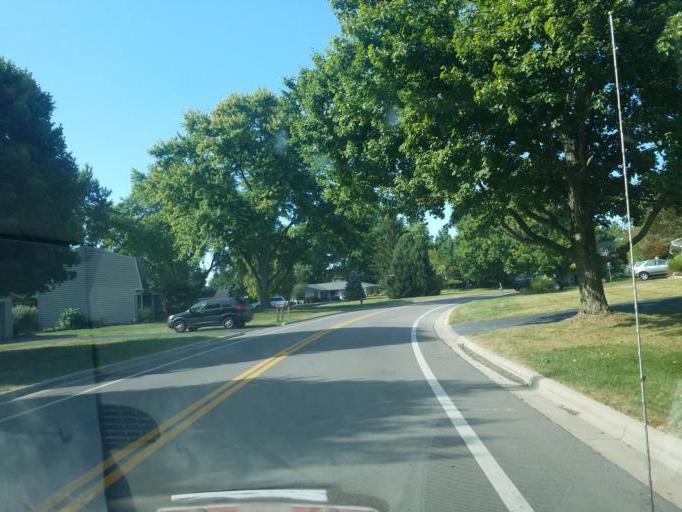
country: US
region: Ohio
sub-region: Franklin County
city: Worthington
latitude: 40.1229
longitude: -83.0444
